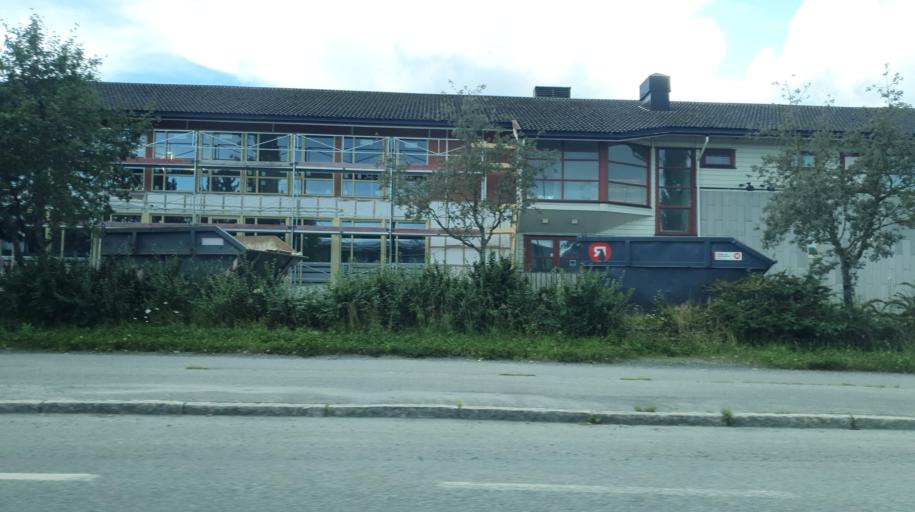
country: NO
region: Nord-Trondelag
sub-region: Levanger
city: Levanger
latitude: 63.7499
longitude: 11.3085
